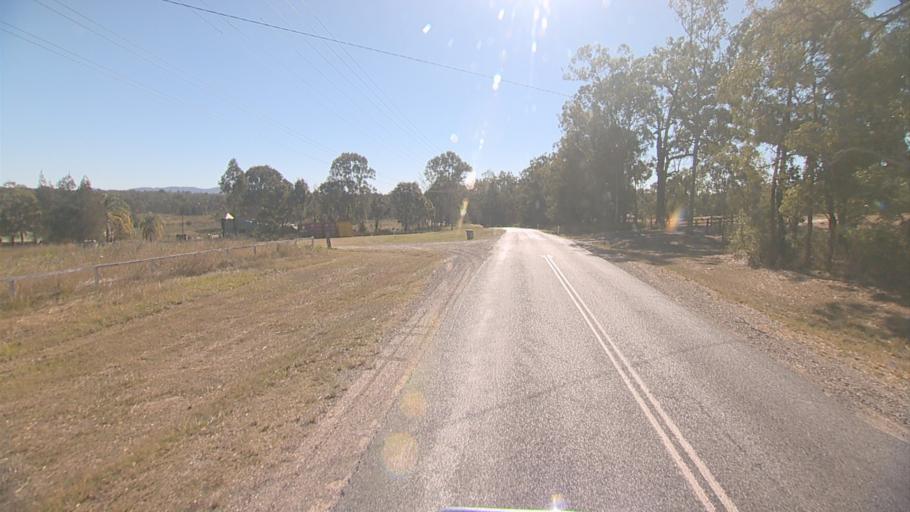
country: AU
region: Queensland
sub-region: Logan
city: North Maclean
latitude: -27.7688
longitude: 153.0021
